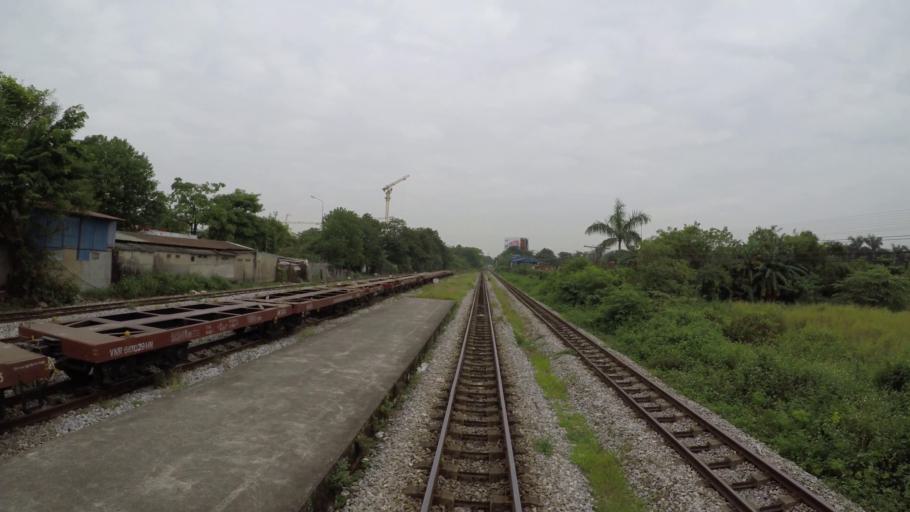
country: VN
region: Hai Phong
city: An Duong
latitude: 20.8829
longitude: 106.6151
